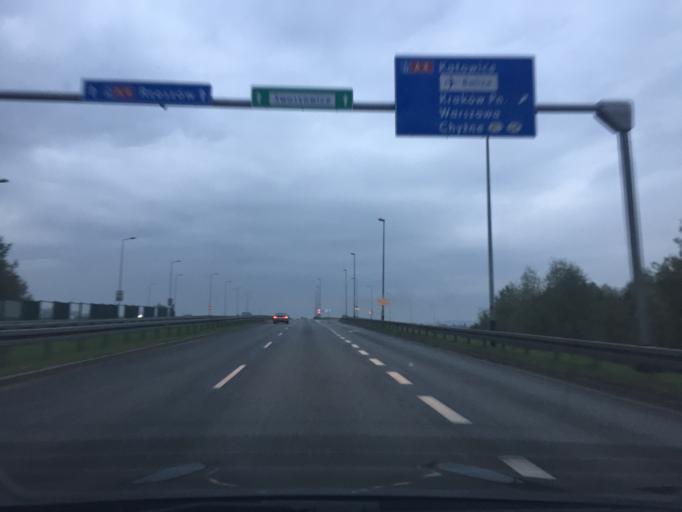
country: PL
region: Lesser Poland Voivodeship
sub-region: Powiat krakowski
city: Wrzasowice
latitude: 50.0039
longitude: 19.9423
